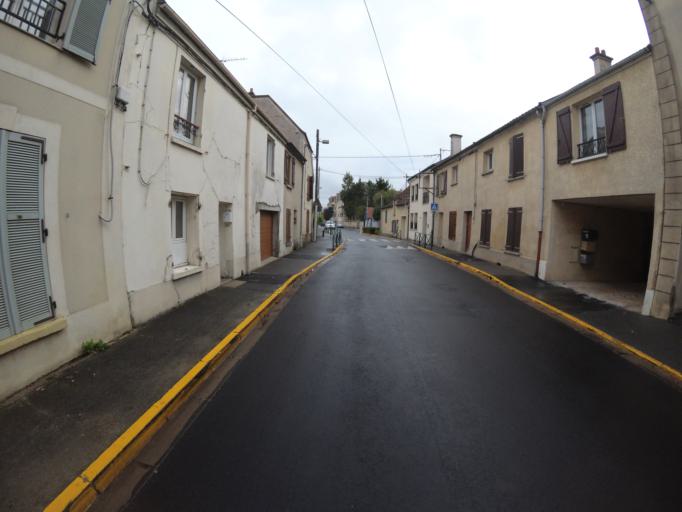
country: FR
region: Ile-de-France
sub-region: Departement de Seine-et-Marne
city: Chanteloup-en-Brie
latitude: 48.8554
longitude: 2.7388
